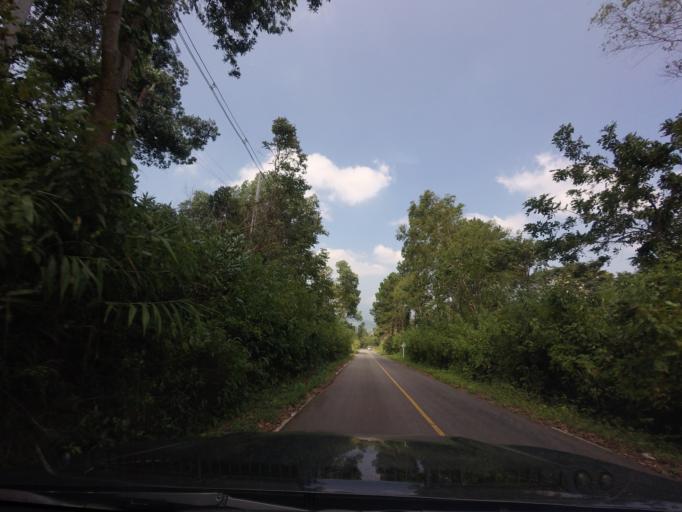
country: TH
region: Loei
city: Na Haeo
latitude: 17.4864
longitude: 100.9048
